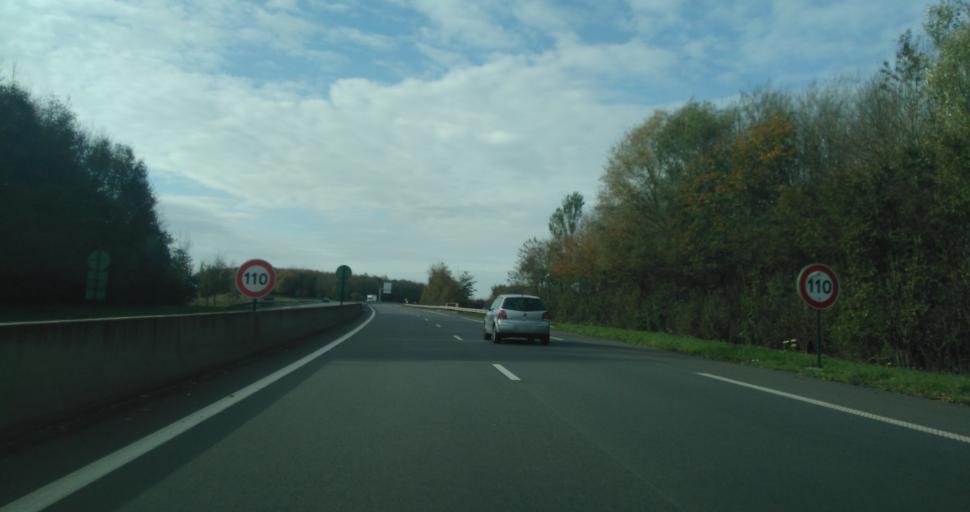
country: FR
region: Nord-Pas-de-Calais
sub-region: Departement du Pas-de-Calais
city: Saint-Pol-sur-Ternoise
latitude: 50.3647
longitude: 2.4041
